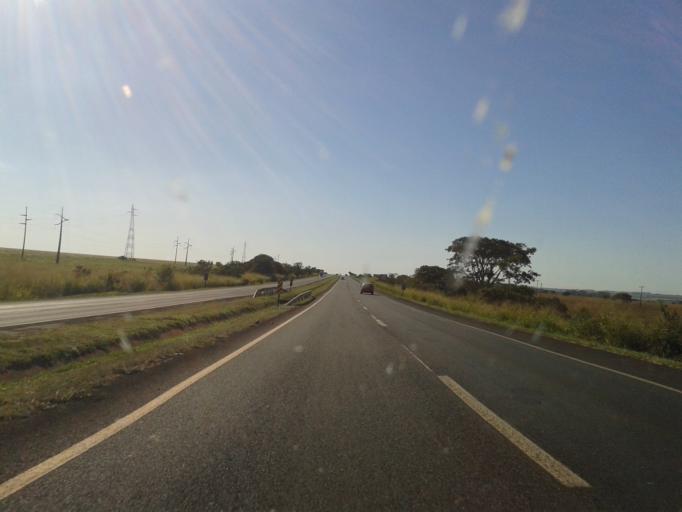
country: BR
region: Minas Gerais
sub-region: Uberlandia
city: Uberlandia
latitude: -19.0600
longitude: -48.1934
